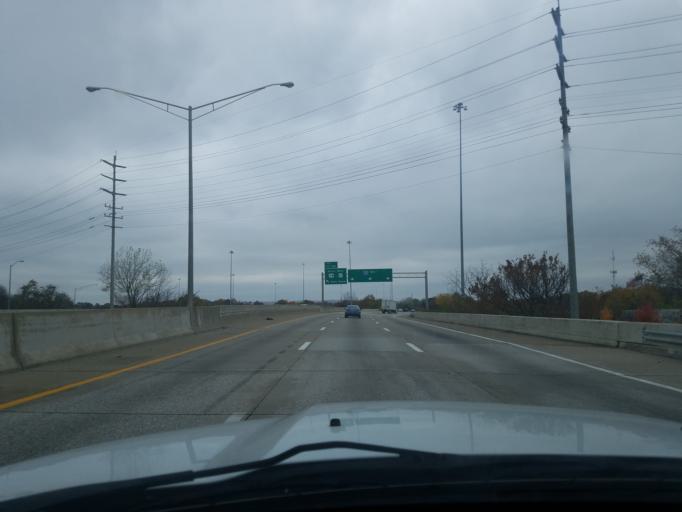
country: US
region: Kentucky
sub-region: Jefferson County
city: Shively
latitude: 38.1858
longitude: -85.8081
